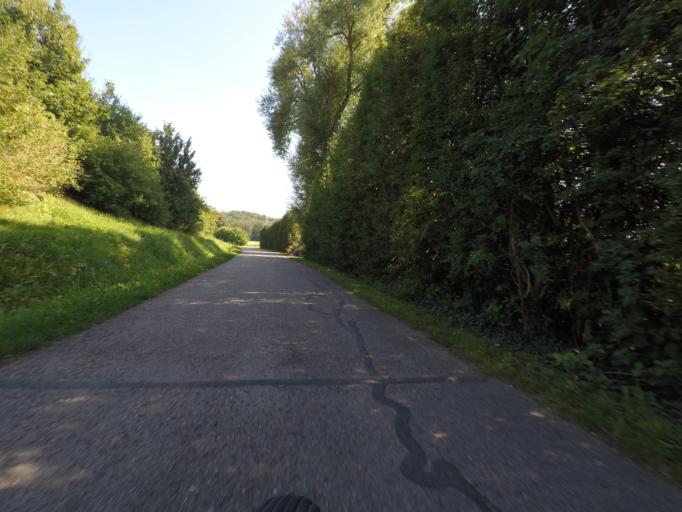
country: DE
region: Baden-Wuerttemberg
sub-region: Regierungsbezirk Stuttgart
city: Hildrizhausen
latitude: 48.6214
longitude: 8.9727
